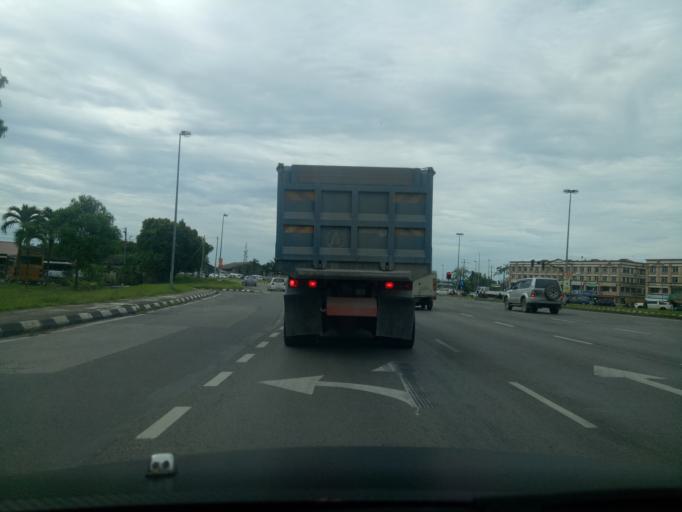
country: MY
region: Sarawak
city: Kuching
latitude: 1.5506
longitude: 110.3872
